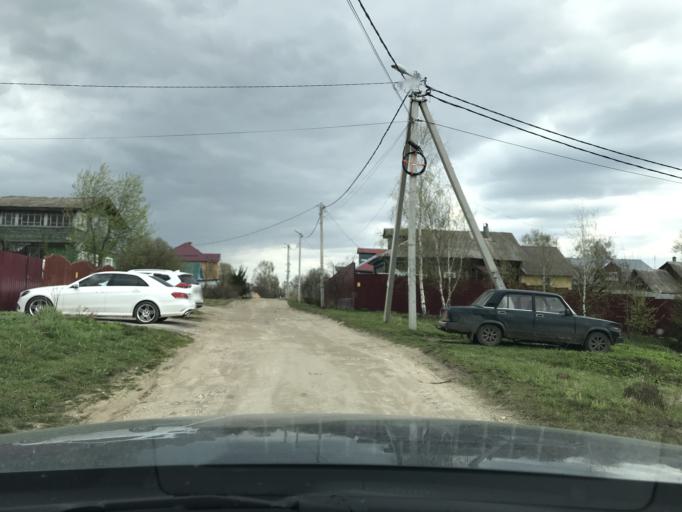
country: RU
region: Vladimir
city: Strunino
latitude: 56.3833
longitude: 38.5935
